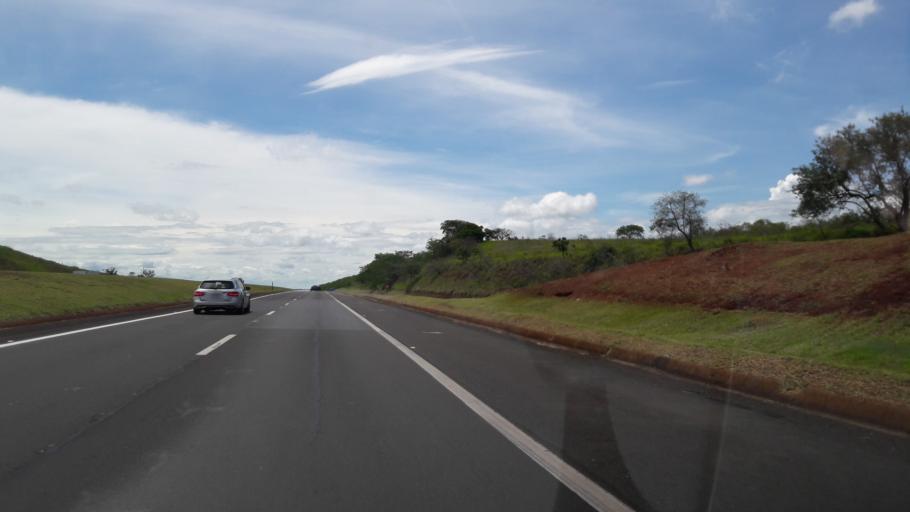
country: BR
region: Sao Paulo
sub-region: Avare
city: Avare
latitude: -22.9598
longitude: -48.8135
